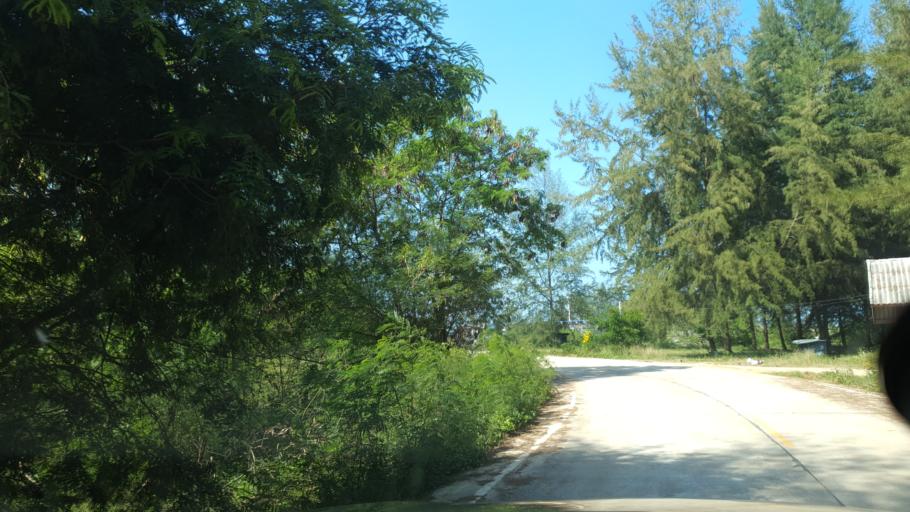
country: TH
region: Surat Thani
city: Tha Chana
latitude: 9.5994
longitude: 99.2093
